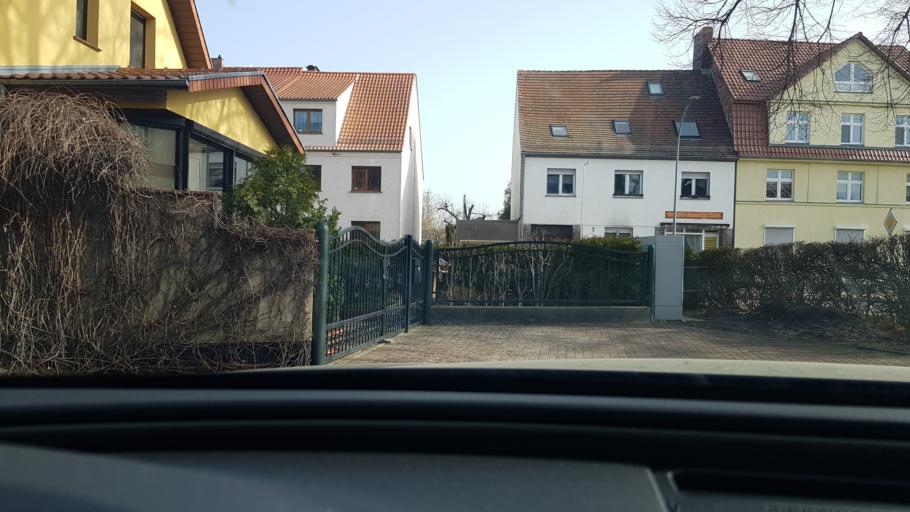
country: DE
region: Brandenburg
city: Guben
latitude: 51.9617
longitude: 14.7017
